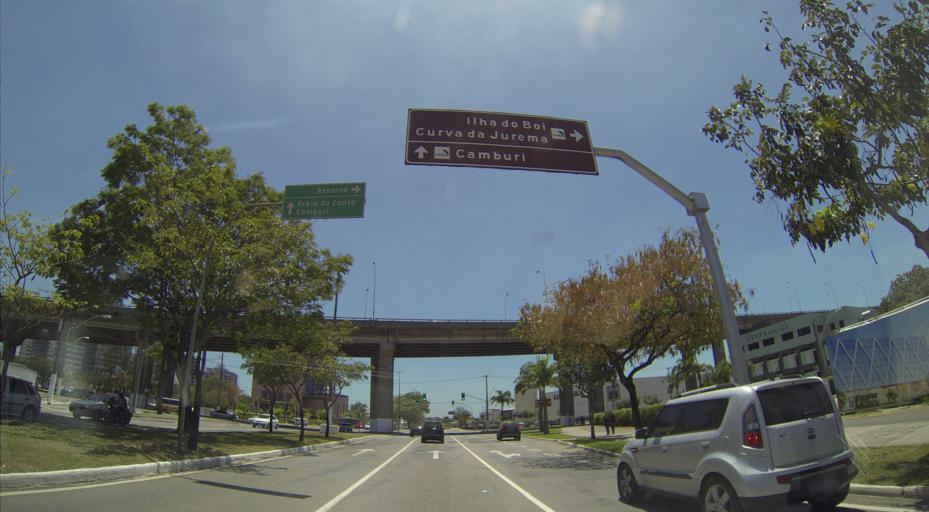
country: BR
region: Espirito Santo
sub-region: Vila Velha
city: Vila Velha
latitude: -20.3145
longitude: -40.2910
